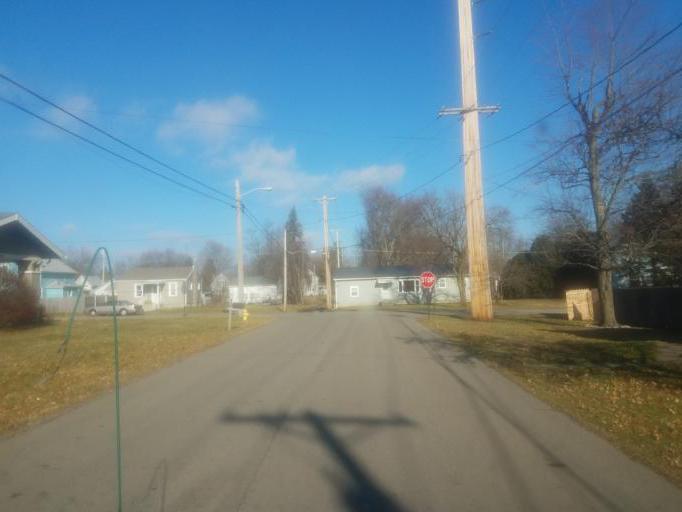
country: US
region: Ohio
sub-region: Crawford County
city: Galion
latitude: 40.7273
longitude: -82.7997
